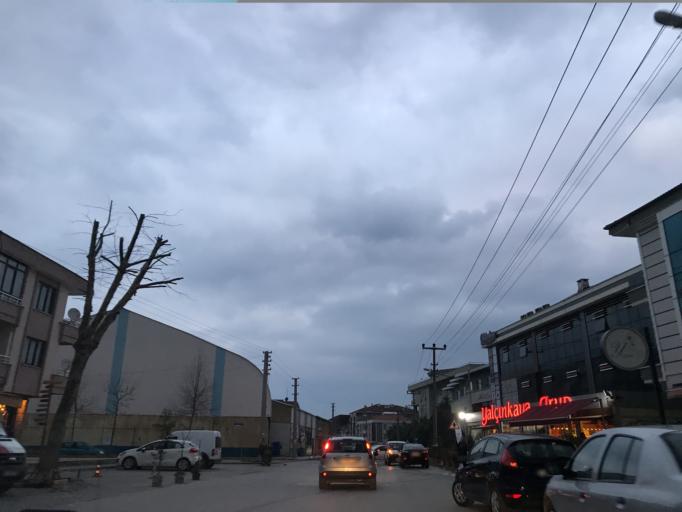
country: TR
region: Yalova
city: Yalova
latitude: 40.6483
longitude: 29.2609
